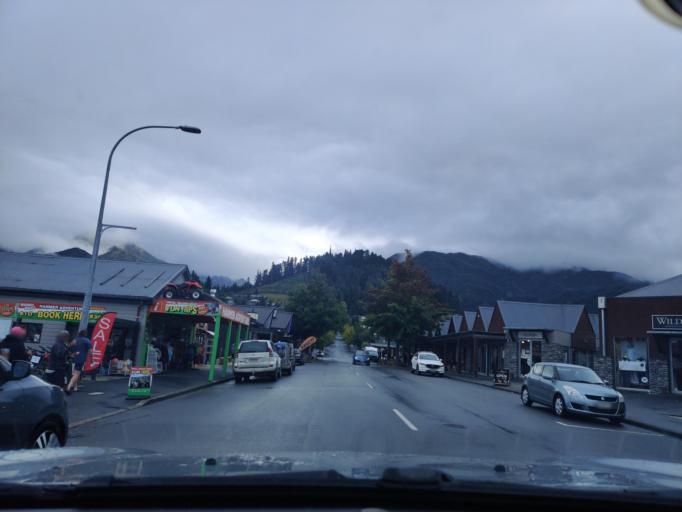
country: NZ
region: Canterbury
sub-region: Hurunui District
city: Amberley
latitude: -42.5207
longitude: 172.8295
